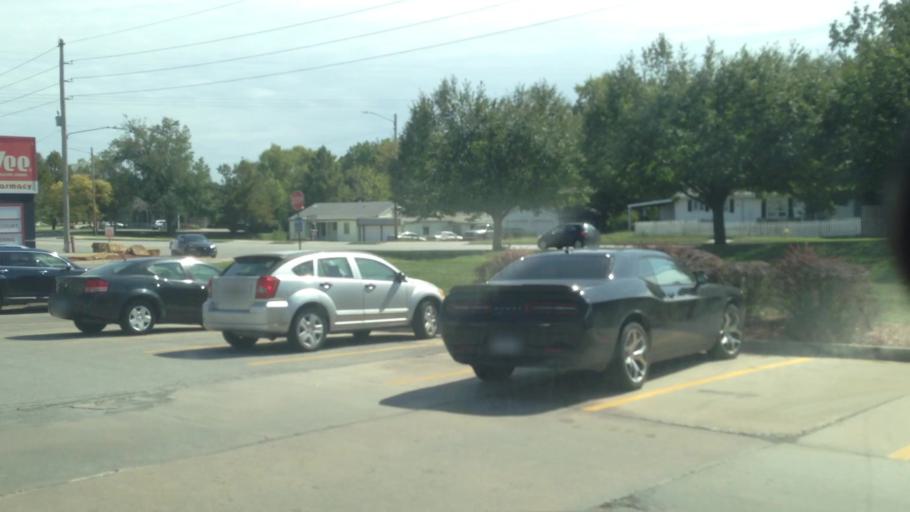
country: US
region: Kansas
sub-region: Douglas County
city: Lawrence
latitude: 38.9720
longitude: -95.2909
